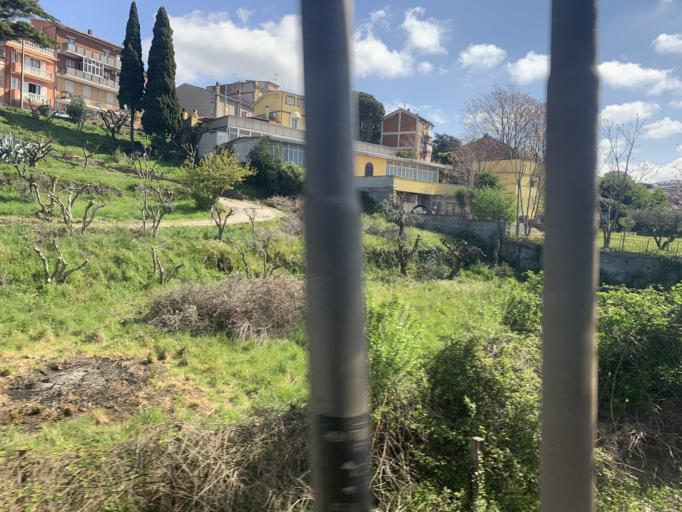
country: IT
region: Latium
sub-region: Citta metropolitana di Roma Capitale
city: Marino
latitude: 41.7710
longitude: 12.6474
